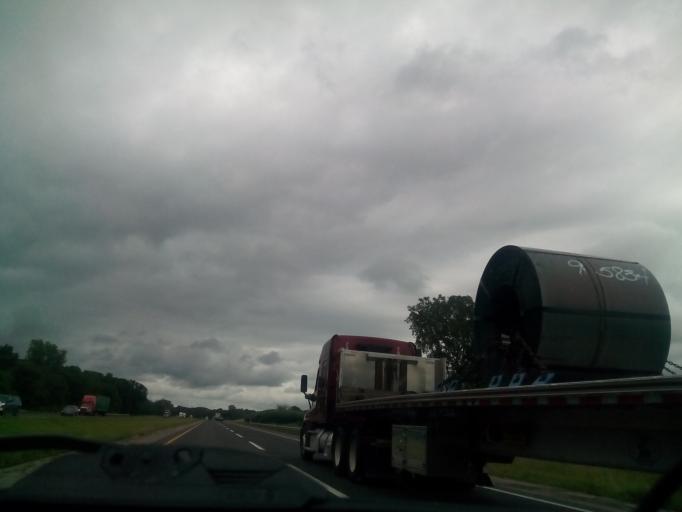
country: US
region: Michigan
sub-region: Branch County
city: Bronson
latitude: 41.7546
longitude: -85.2463
